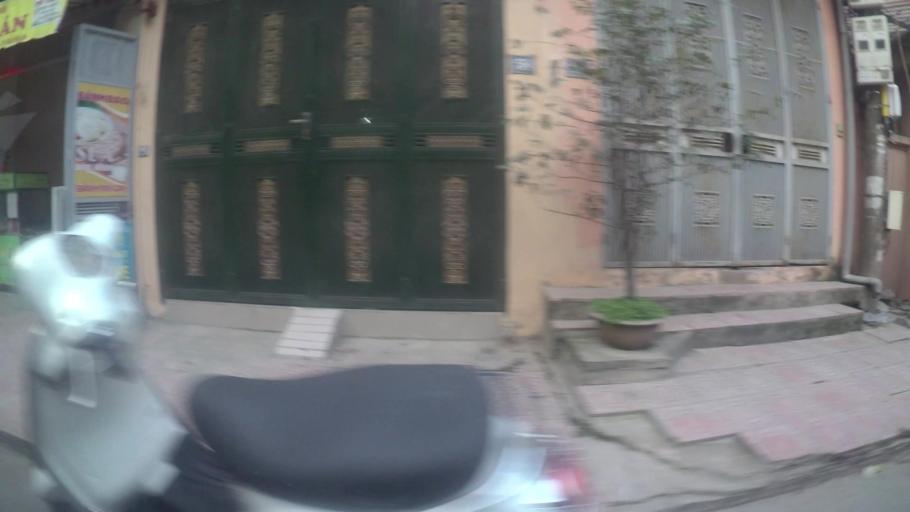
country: VN
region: Ha Noi
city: Cau Giay
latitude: 21.0491
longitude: 105.7943
